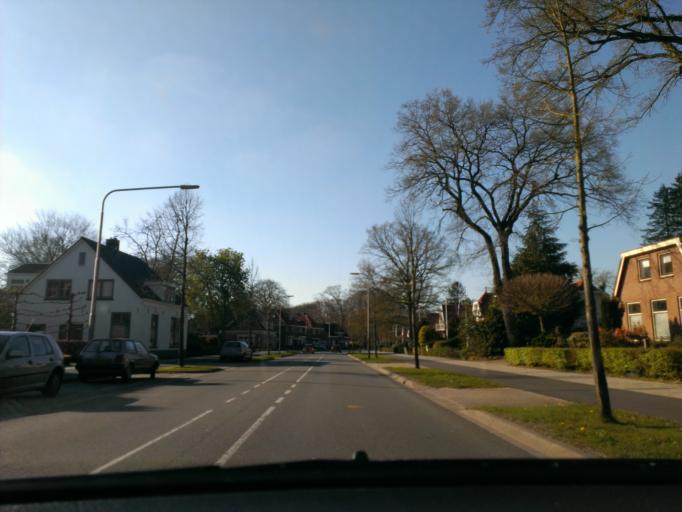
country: NL
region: Overijssel
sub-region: Gemeente Twenterand
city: Den Ham
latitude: 52.5086
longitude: 6.4207
